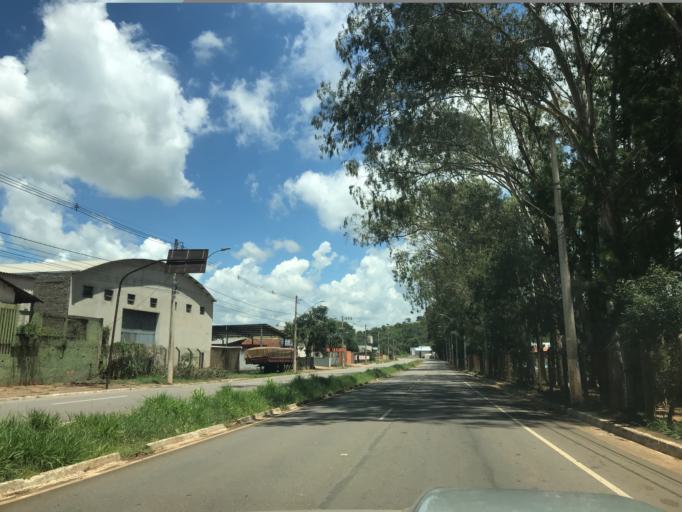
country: BR
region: Minas Gerais
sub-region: Tres Coracoes
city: Tres Coracoes
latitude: -21.6626
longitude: -45.2836
